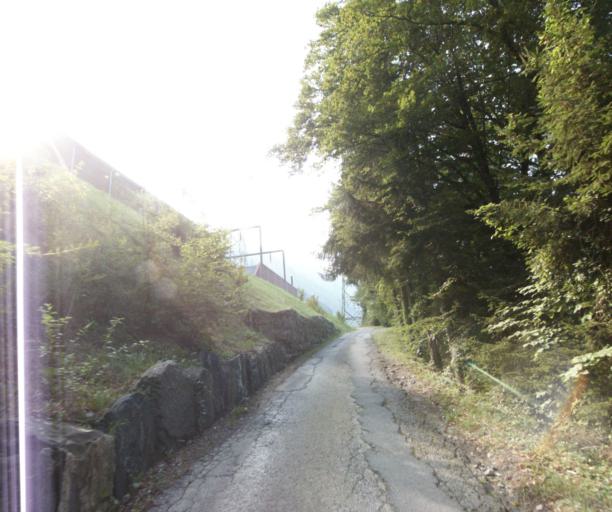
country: CH
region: Vaud
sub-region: Aigle District
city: Villeneuve
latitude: 46.4067
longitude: 6.9388
